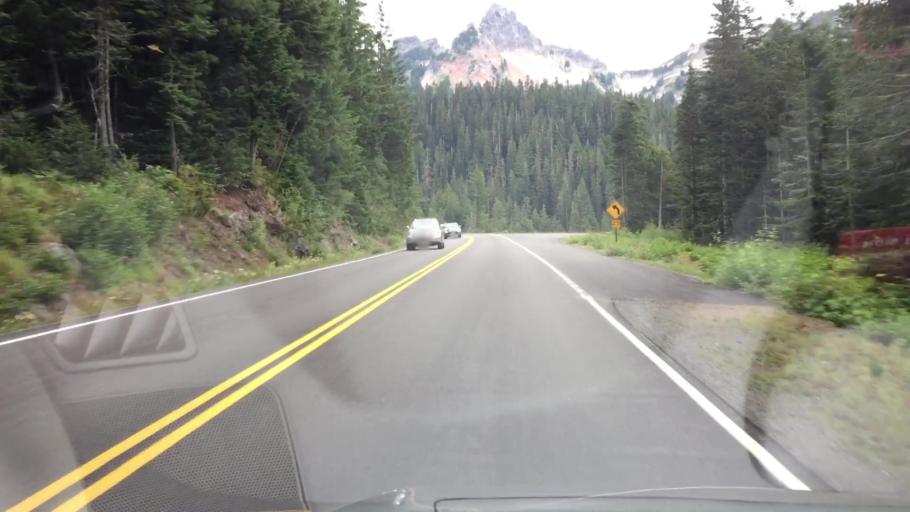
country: US
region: Washington
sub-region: Pierce County
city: Buckley
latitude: 46.7747
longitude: -121.7522
